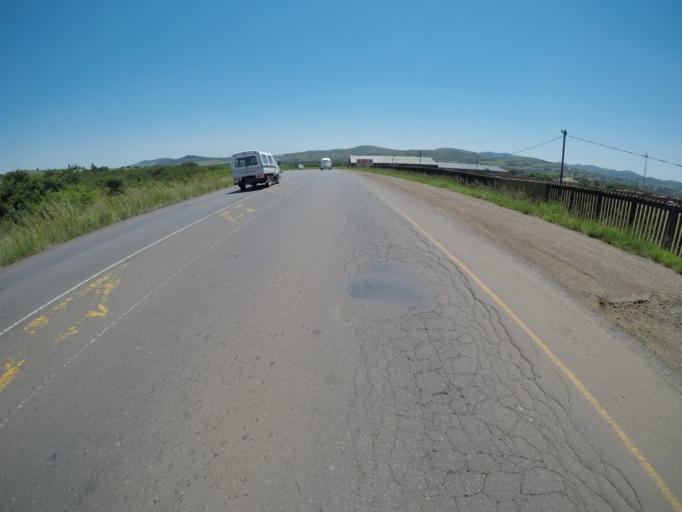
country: ZA
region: KwaZulu-Natal
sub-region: uThungulu District Municipality
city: Empangeni
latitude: -28.7258
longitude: 31.8671
